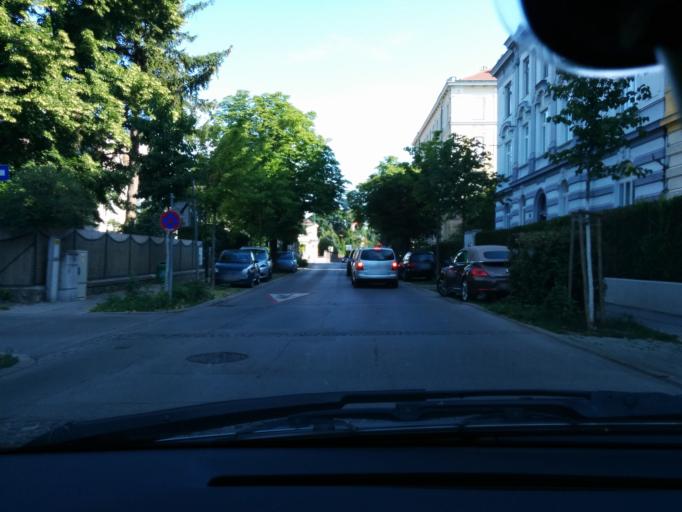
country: AT
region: Lower Austria
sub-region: Politischer Bezirk Modling
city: Modling
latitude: 48.0816
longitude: 16.2873
